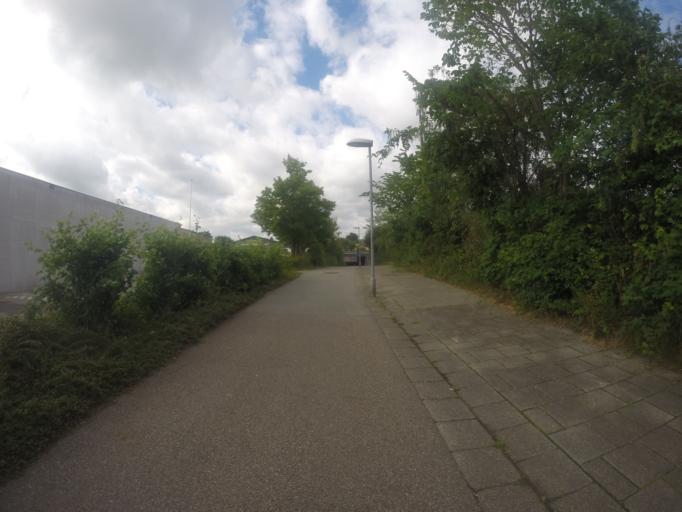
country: DK
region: Capital Region
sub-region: Hoje-Taastrup Kommune
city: Taastrup
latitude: 55.6568
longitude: 12.2969
